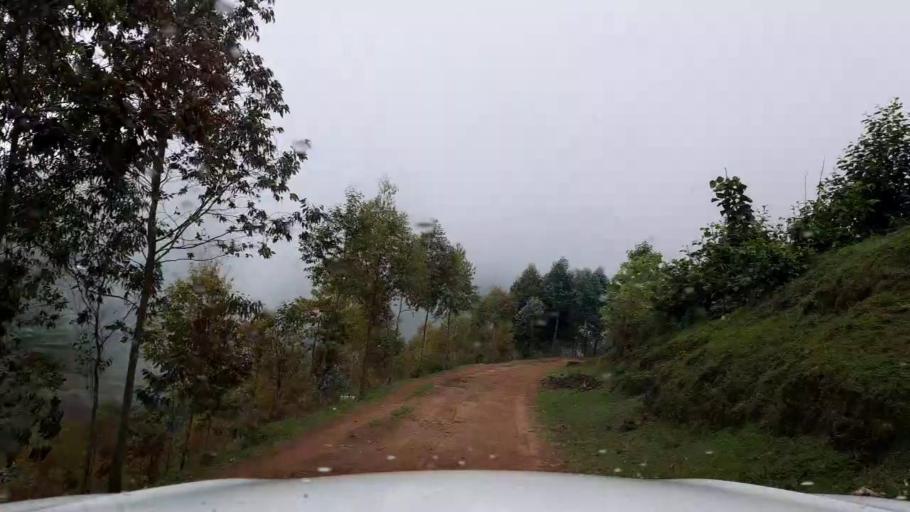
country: RW
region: Northern Province
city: Musanze
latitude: -1.5962
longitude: 29.7913
